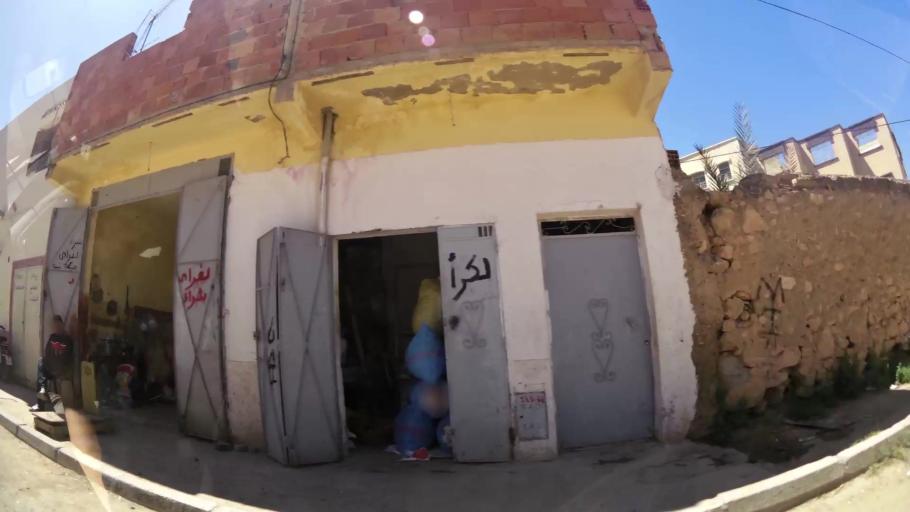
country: MA
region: Oriental
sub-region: Oujda-Angad
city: Oujda
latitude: 34.6593
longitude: -1.8820
